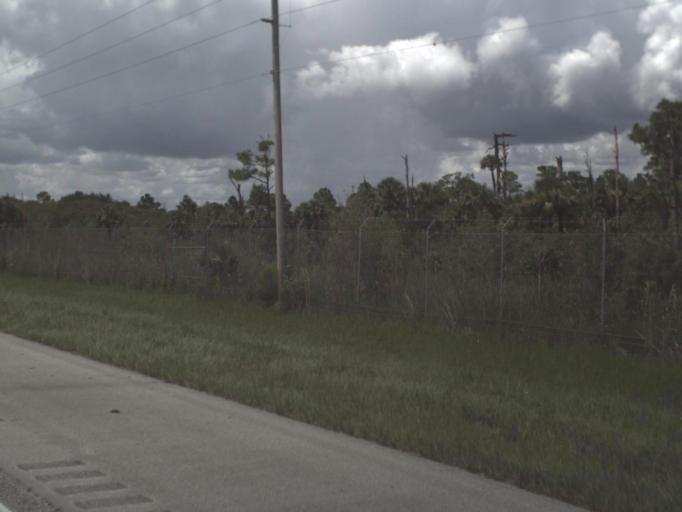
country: US
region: Florida
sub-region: Collier County
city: Immokalee
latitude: 26.1551
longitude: -81.3225
